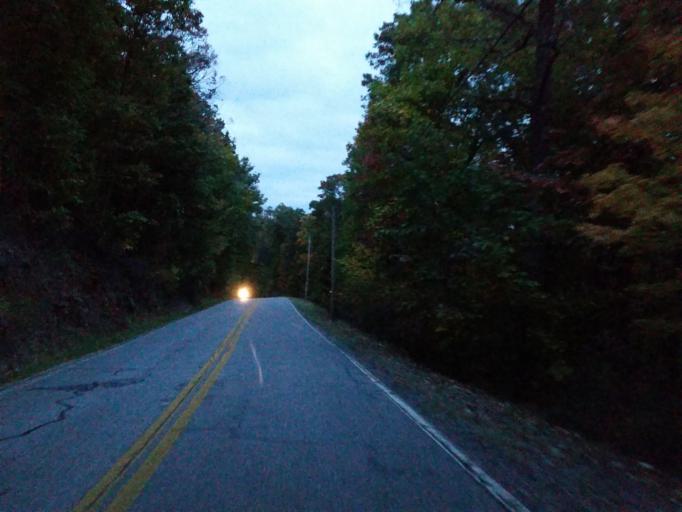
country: US
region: Georgia
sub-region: Lumpkin County
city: Dahlonega
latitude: 34.6361
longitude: -83.9573
